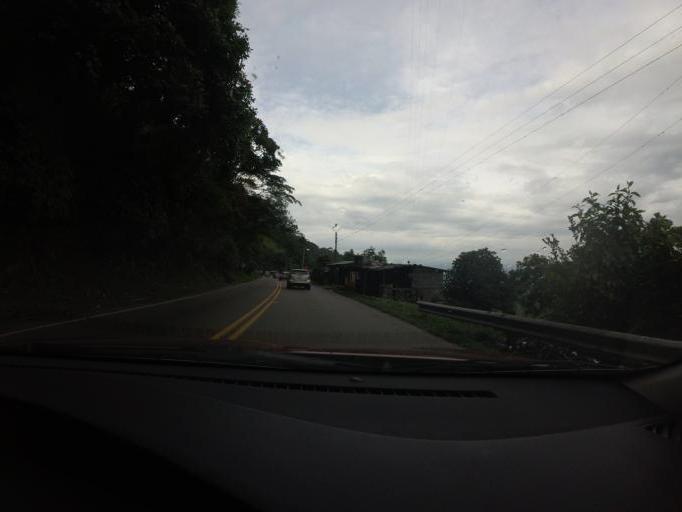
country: CO
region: Cundinamarca
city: Villeta
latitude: 5.0052
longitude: -74.5357
